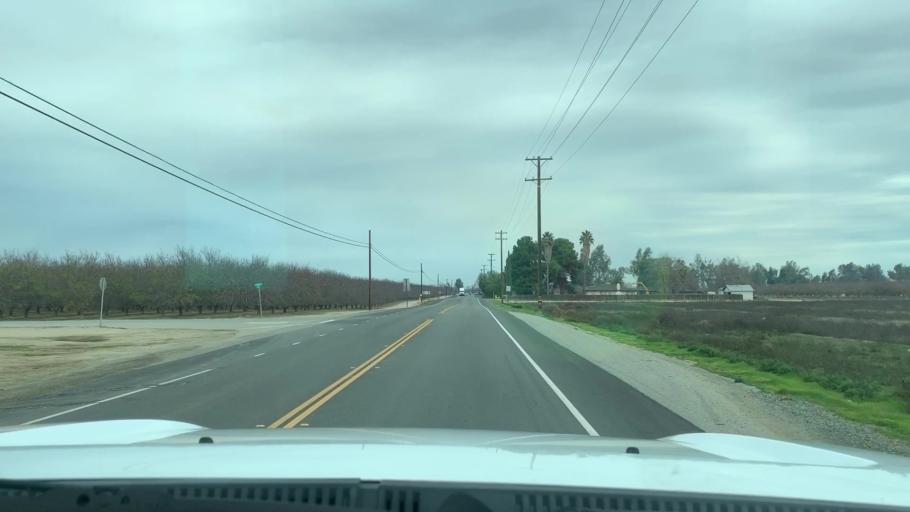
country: US
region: California
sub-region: Kern County
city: Shafter
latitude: 35.4219
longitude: -119.2519
